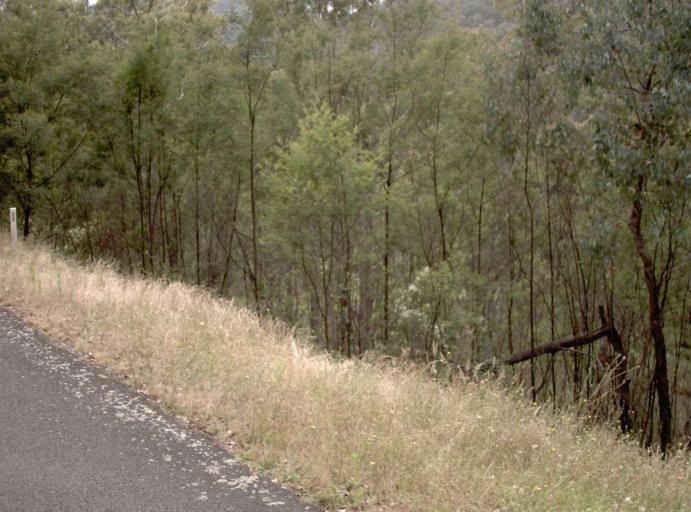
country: AU
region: Victoria
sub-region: Wellington
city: Heyfield
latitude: -37.7420
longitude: 146.6677
